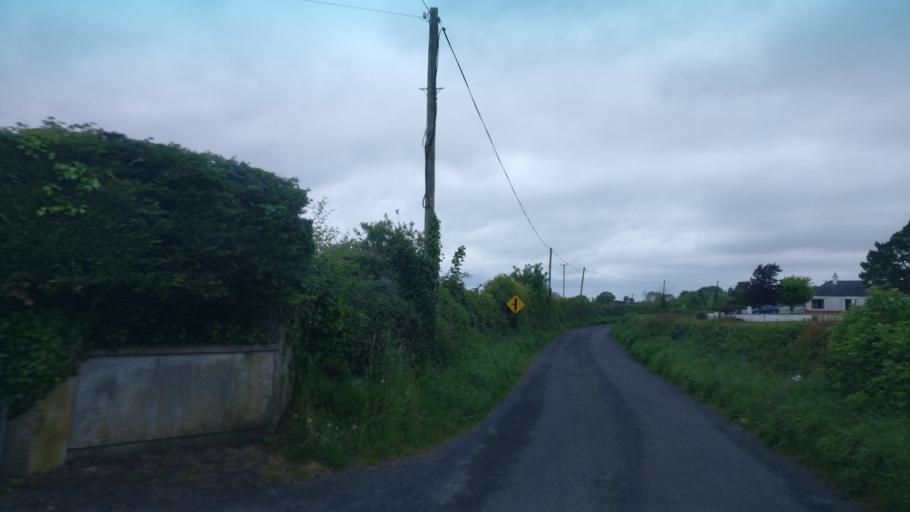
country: IE
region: Connaught
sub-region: County Galway
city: Portumna
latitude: 53.1165
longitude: -8.2890
